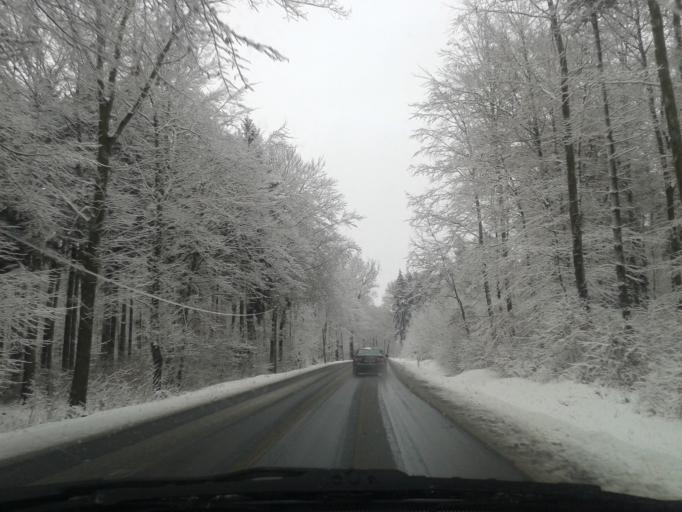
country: DE
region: Saxony
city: Arnsdorf
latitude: 51.0720
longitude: 13.9978
